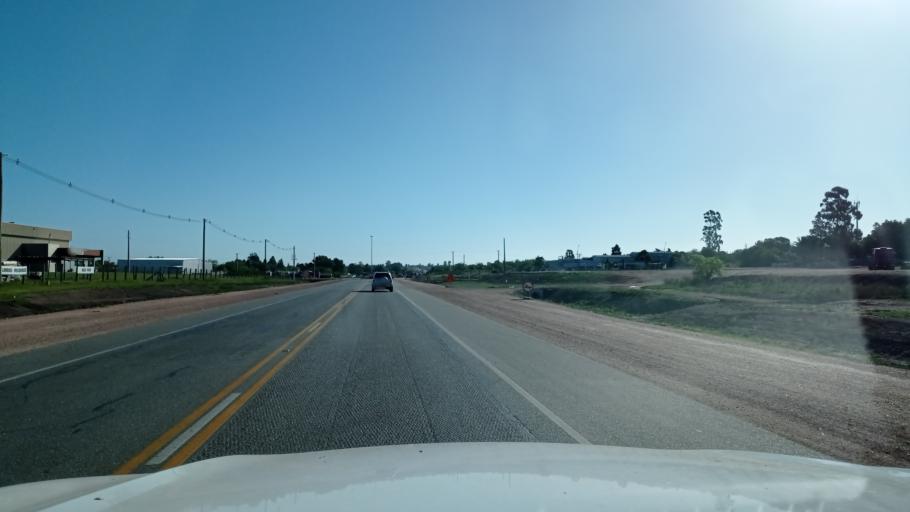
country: UY
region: Canelones
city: Pando
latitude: -34.7272
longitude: -55.9516
